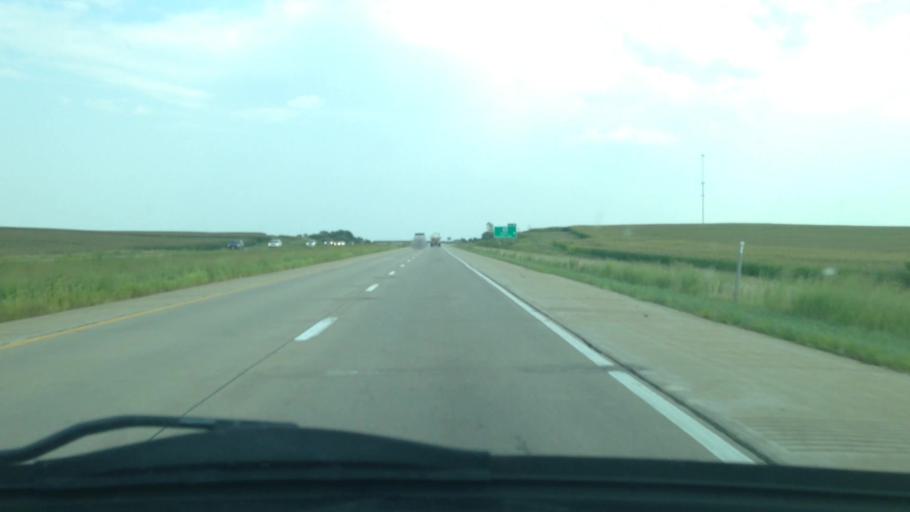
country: US
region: Iowa
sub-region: Buchanan County
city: Jesup
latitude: 42.3574
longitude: -92.0745
